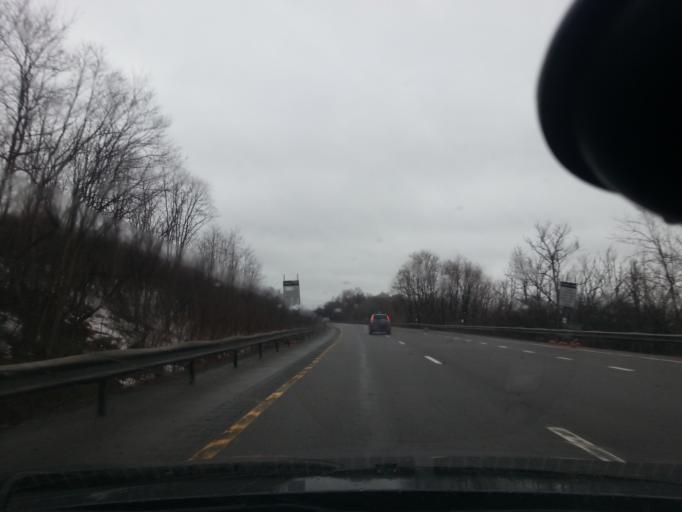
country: US
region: New York
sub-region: Onondaga County
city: Nedrow
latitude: 42.9998
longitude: -76.1352
